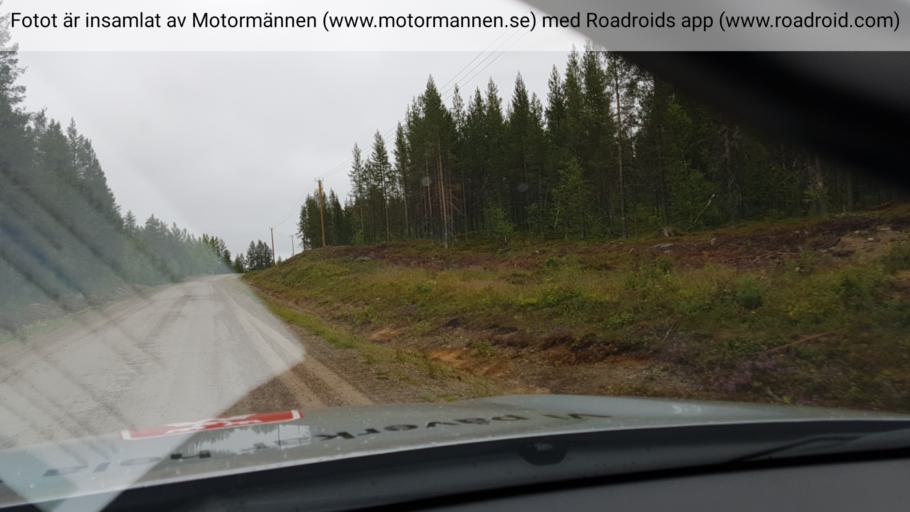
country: SE
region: Norrbotten
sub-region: Gallivare Kommun
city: Gaellivare
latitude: 66.7195
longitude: 20.5297
